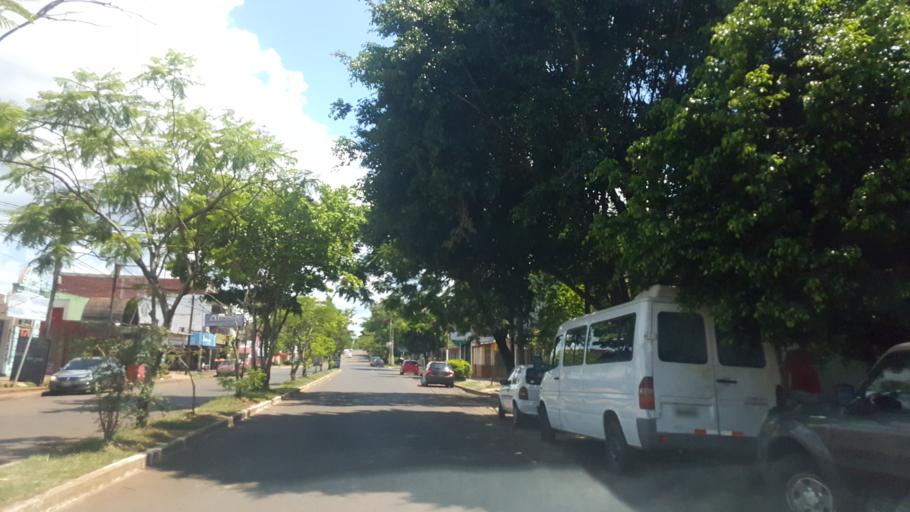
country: AR
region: Misiones
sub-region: Departamento de Capital
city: Posadas
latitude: -27.3647
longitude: -55.9466
